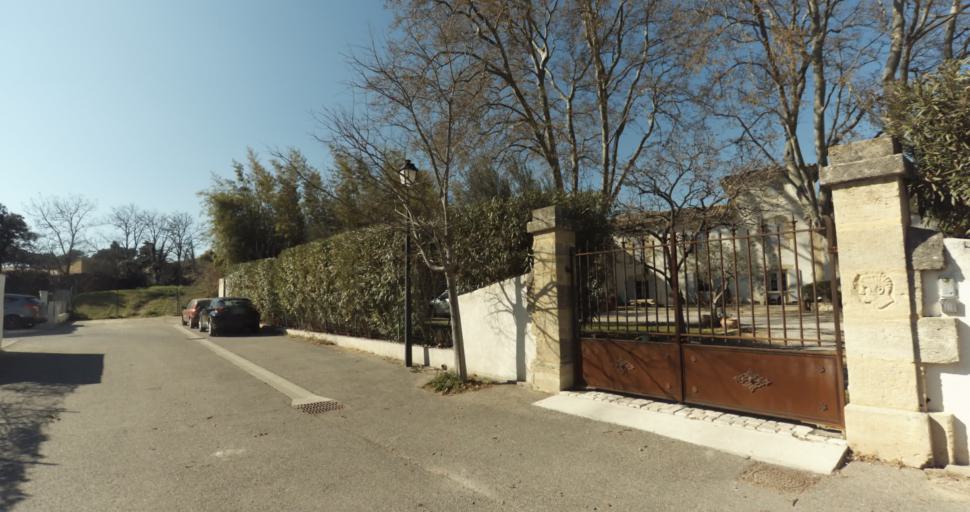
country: FR
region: Provence-Alpes-Cote d'Azur
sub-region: Departement des Bouches-du-Rhone
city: Pelissanne
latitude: 43.6389
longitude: 5.1386
